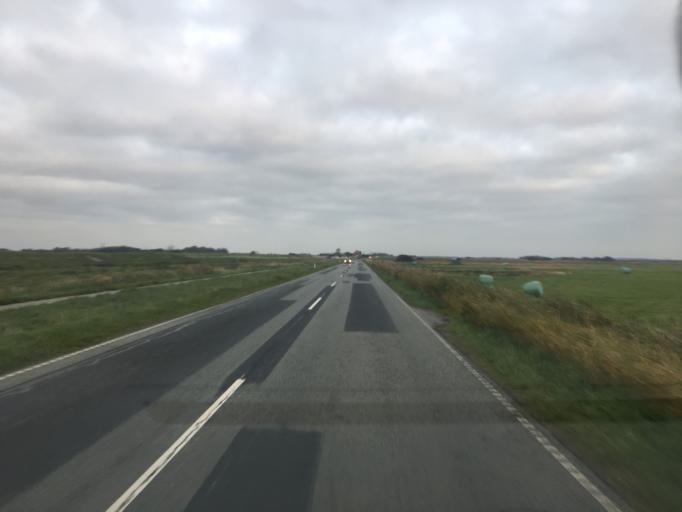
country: DE
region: Schleswig-Holstein
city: Rodenas
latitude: 54.9628
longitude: 8.7203
